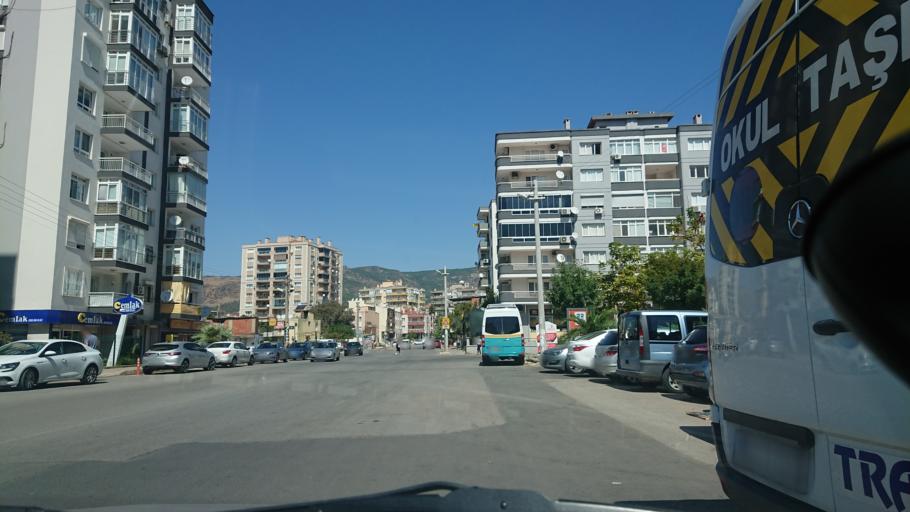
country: TR
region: Izmir
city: Karsiyaka
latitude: 38.4795
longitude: 27.1176
